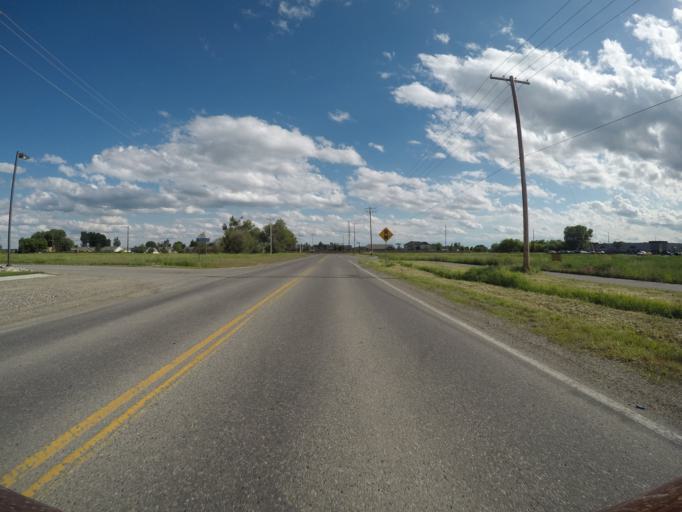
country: US
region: Montana
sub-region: Yellowstone County
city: Billings
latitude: 45.7856
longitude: -108.6527
